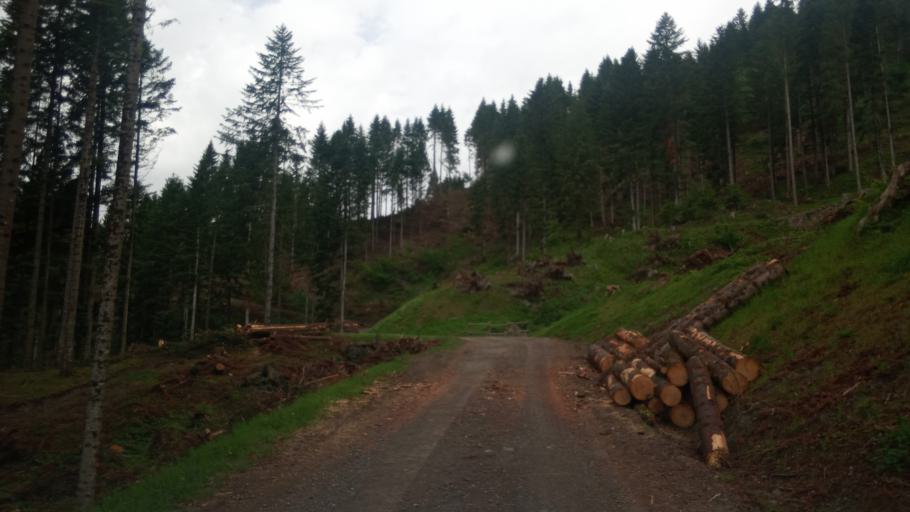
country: IT
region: Friuli Venezia Giulia
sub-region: Provincia di Udine
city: Paluzza
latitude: 46.5689
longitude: 13.0198
